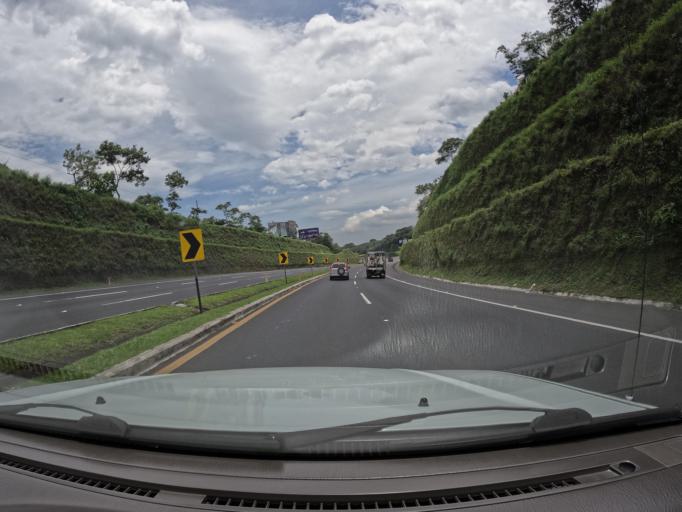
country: GT
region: Escuintla
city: Palin
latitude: 14.3947
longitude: -90.7357
